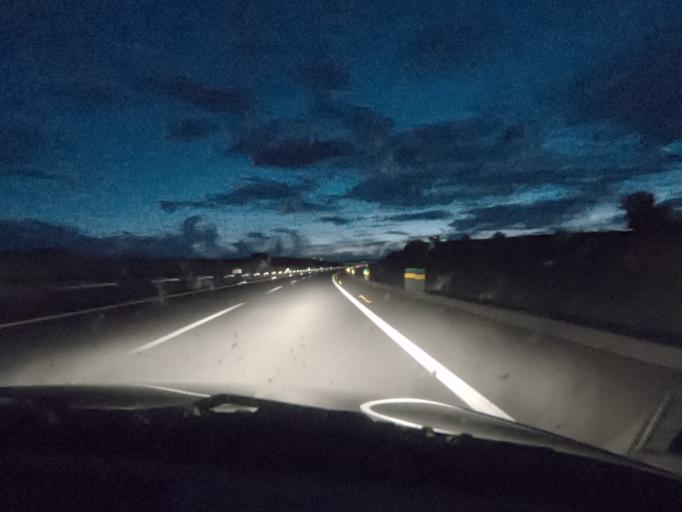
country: ES
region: Extremadura
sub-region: Provincia de Caceres
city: Riolobos
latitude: 39.9736
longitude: -6.3400
